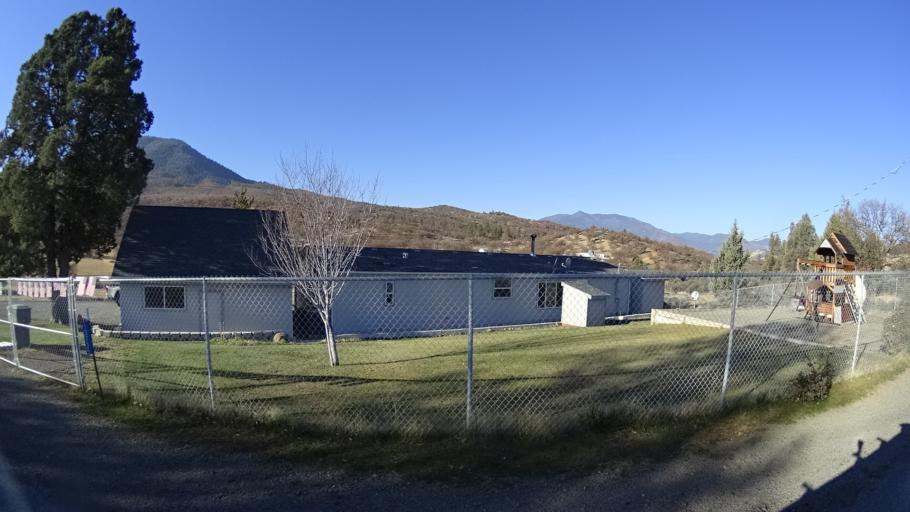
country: US
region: California
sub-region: Siskiyou County
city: Montague
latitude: 41.8909
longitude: -122.4893
